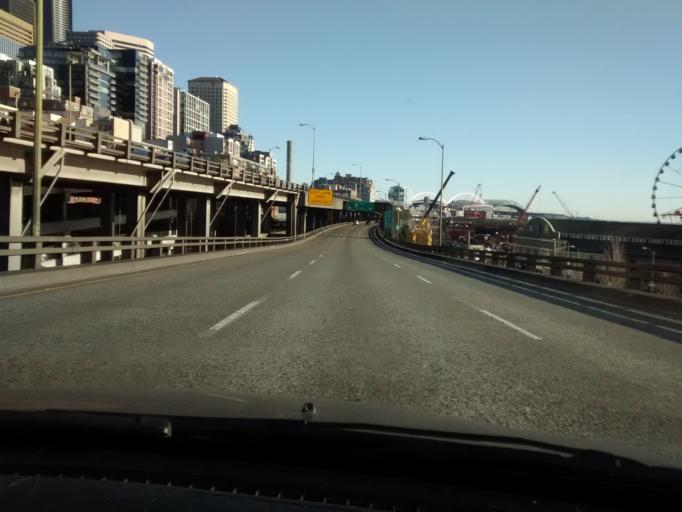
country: US
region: Washington
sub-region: King County
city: Seattle
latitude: 47.6090
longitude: -122.3431
